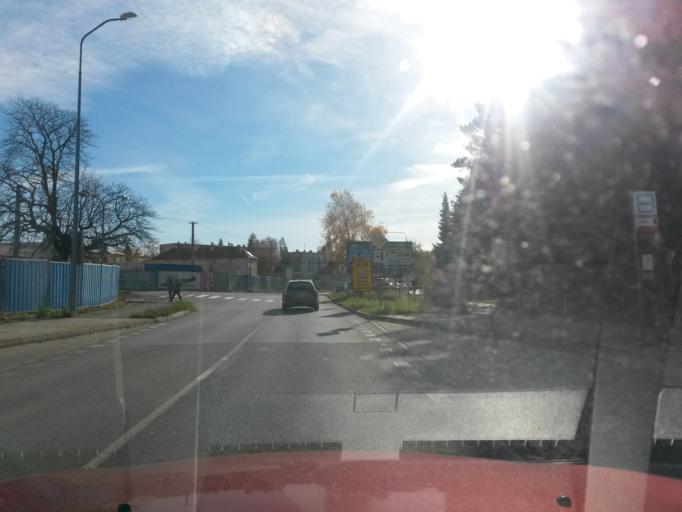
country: SK
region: Presovsky
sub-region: Okres Presov
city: Presov
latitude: 48.9932
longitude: 21.2402
